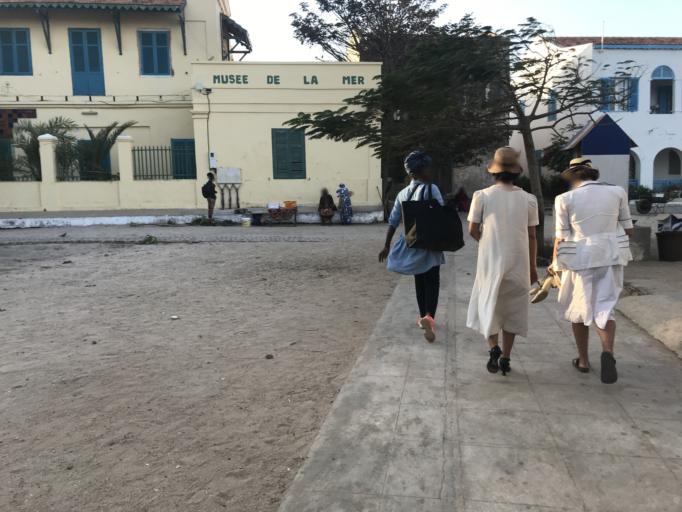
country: SN
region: Dakar
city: Dakar
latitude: 14.6684
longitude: -17.3996
